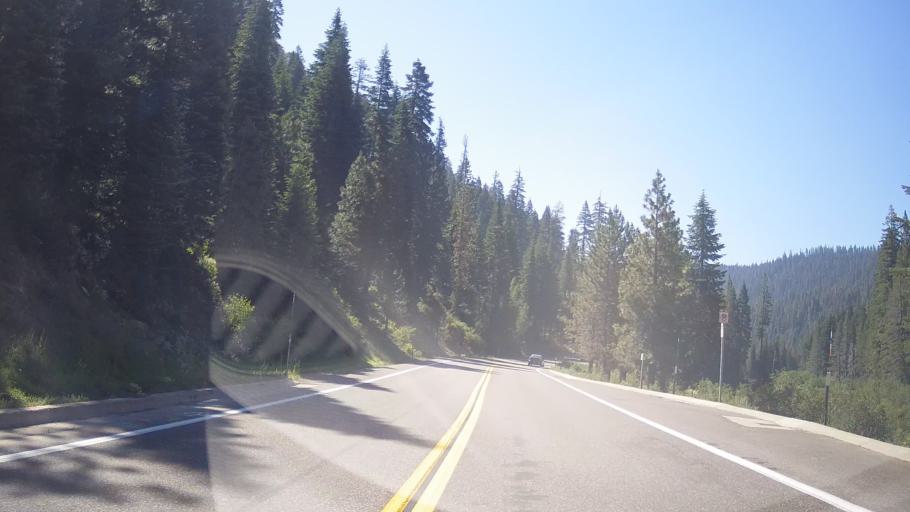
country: US
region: California
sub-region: Placer County
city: Sunnyside-Tahoe City
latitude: 39.1784
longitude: -120.1915
